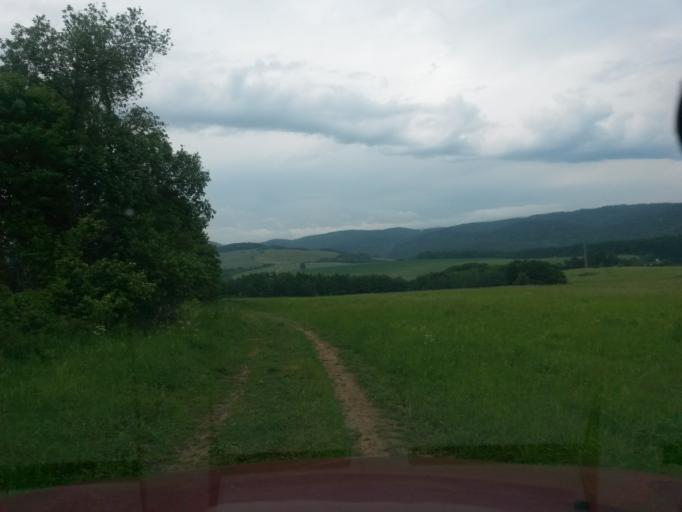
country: SK
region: Kosicky
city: Kosice
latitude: 48.7179
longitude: 21.1506
